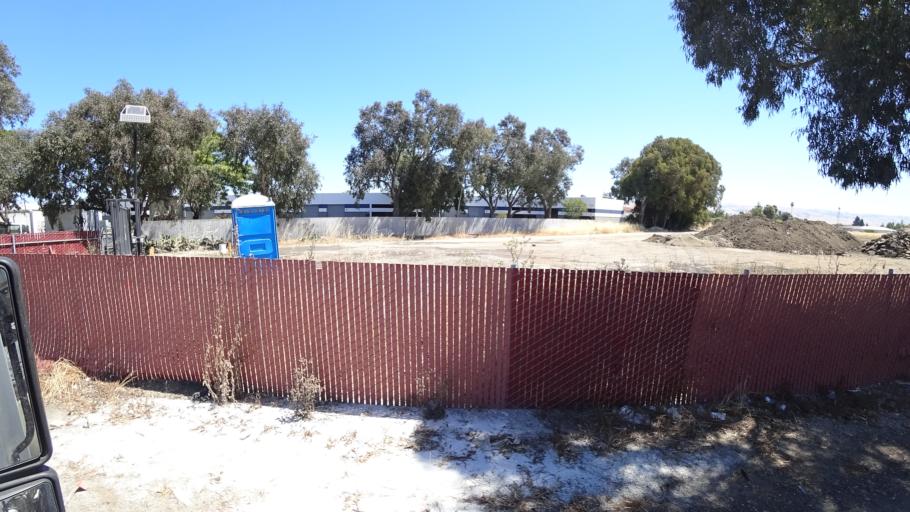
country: US
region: California
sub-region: Alameda County
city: Hayward
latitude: 37.6175
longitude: -122.0941
